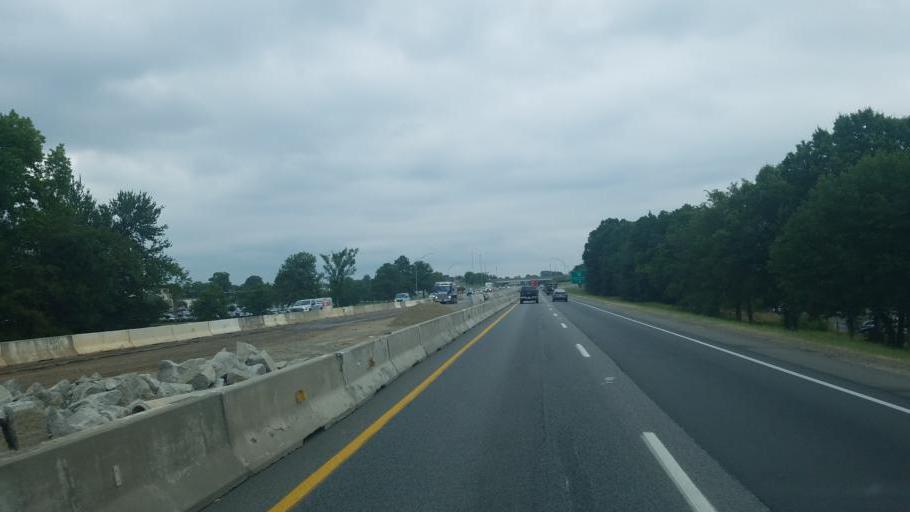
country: US
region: North Carolina
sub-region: Mecklenburg County
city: Cornelius
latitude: 35.4773
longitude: -80.8747
